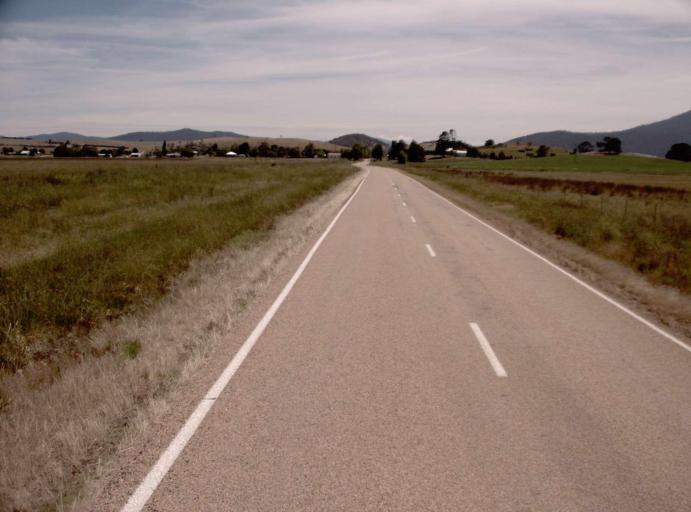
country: AU
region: Victoria
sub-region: Alpine
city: Mount Beauty
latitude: -36.9640
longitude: 147.7033
